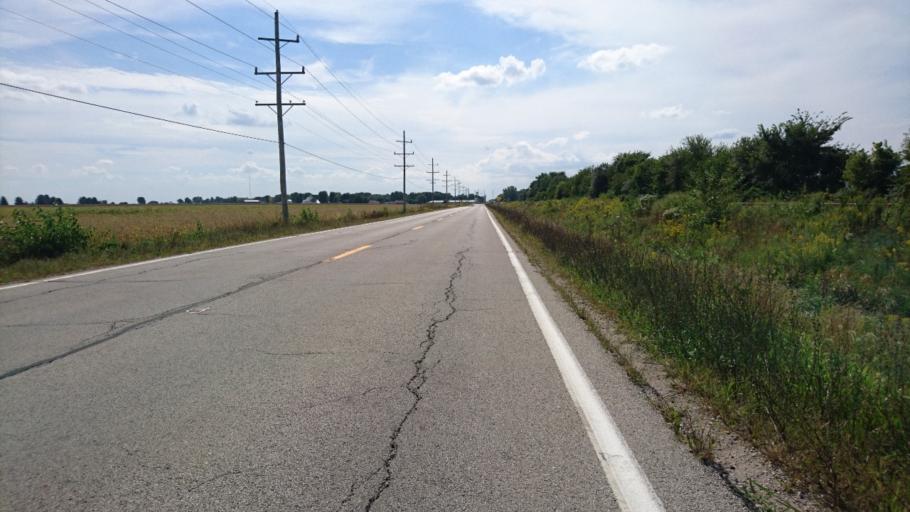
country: US
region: Illinois
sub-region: Grundy County
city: Gardner
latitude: 41.1968
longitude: -88.2965
